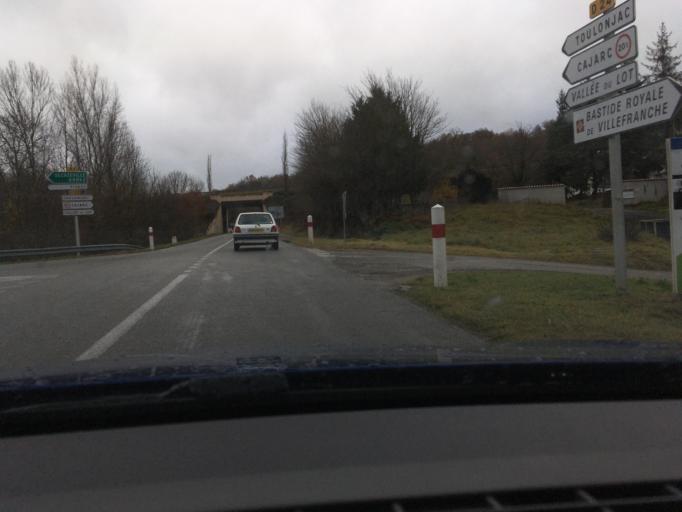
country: FR
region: Midi-Pyrenees
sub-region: Departement de l'Aveyron
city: Villefranche-de-Rouergue
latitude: 44.3734
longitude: 2.0142
